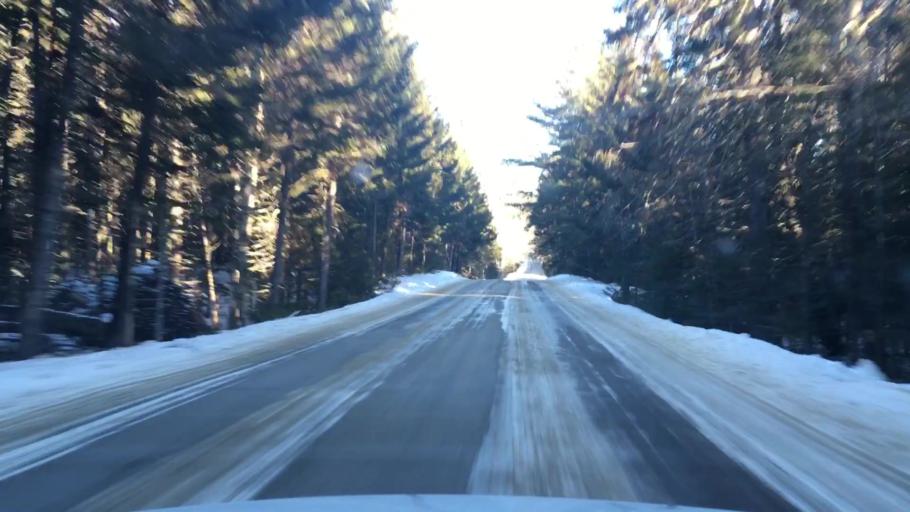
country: US
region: Maine
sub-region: Hancock County
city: Castine
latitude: 44.3600
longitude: -68.7570
